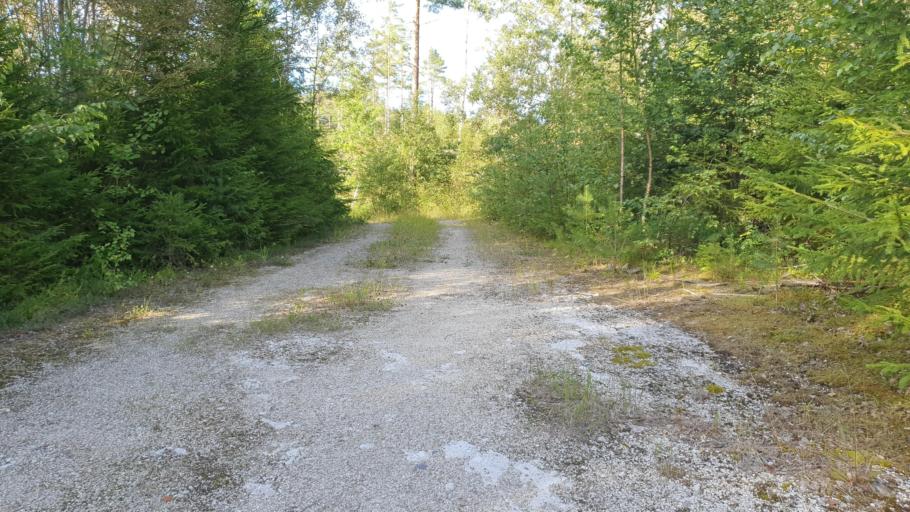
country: SE
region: Vaestra Goetaland
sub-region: Fargelanda Kommun
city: Faergelanda
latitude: 58.5312
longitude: 12.0771
